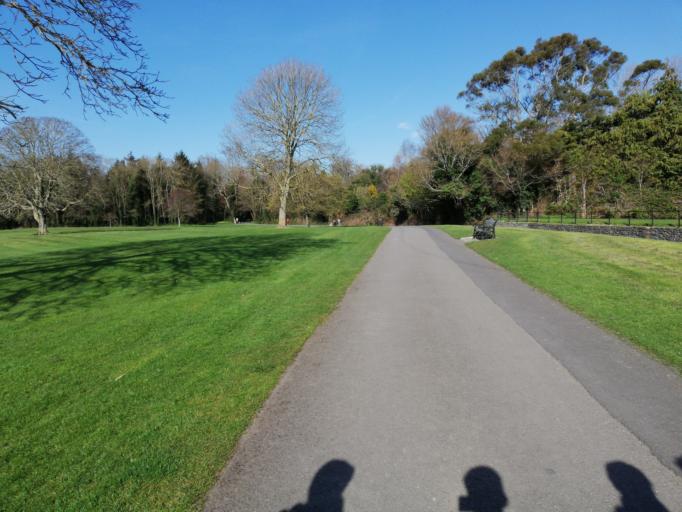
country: IE
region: Leinster
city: Malahide
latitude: 53.4439
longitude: -6.1657
